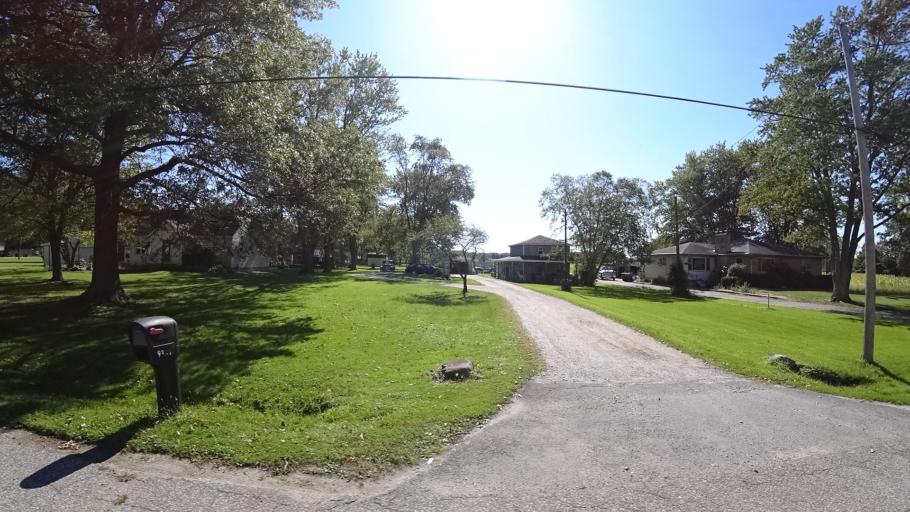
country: US
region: Indiana
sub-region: LaPorte County
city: Trail Creek
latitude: 41.6803
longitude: -86.8813
